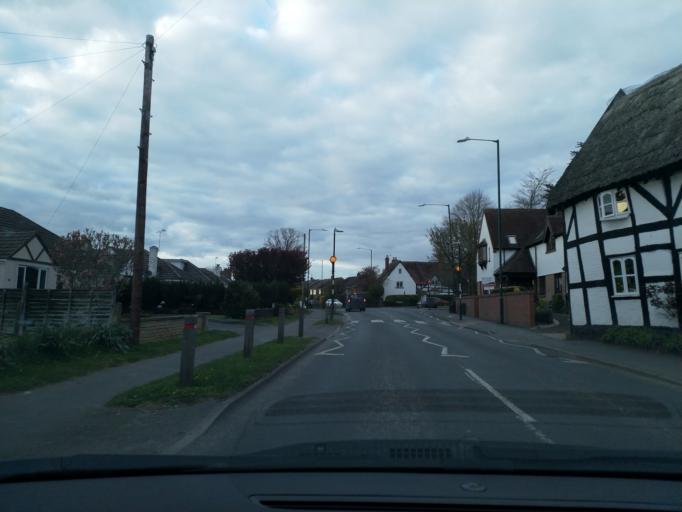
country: GB
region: England
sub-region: Warwickshire
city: Royal Leamington Spa
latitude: 52.2700
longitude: -1.5218
